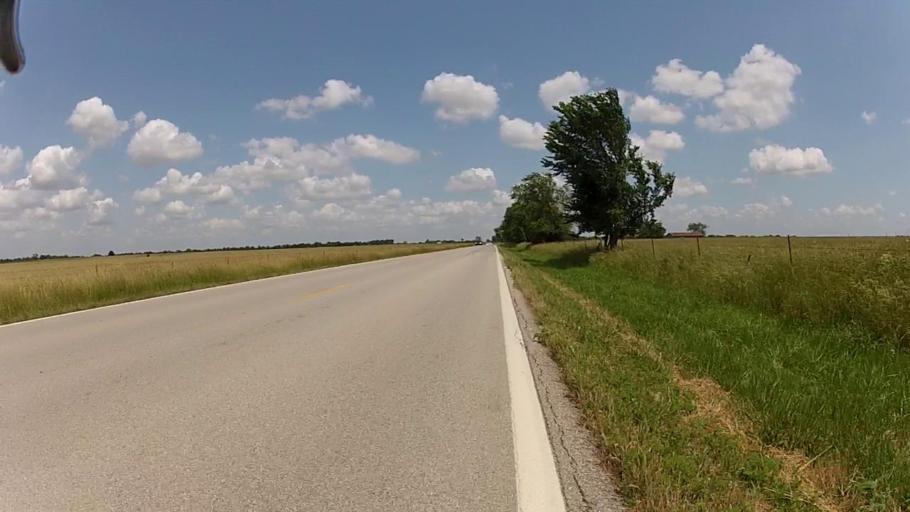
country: US
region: Kansas
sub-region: Labette County
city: Altamont
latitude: 37.1925
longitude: -95.3637
